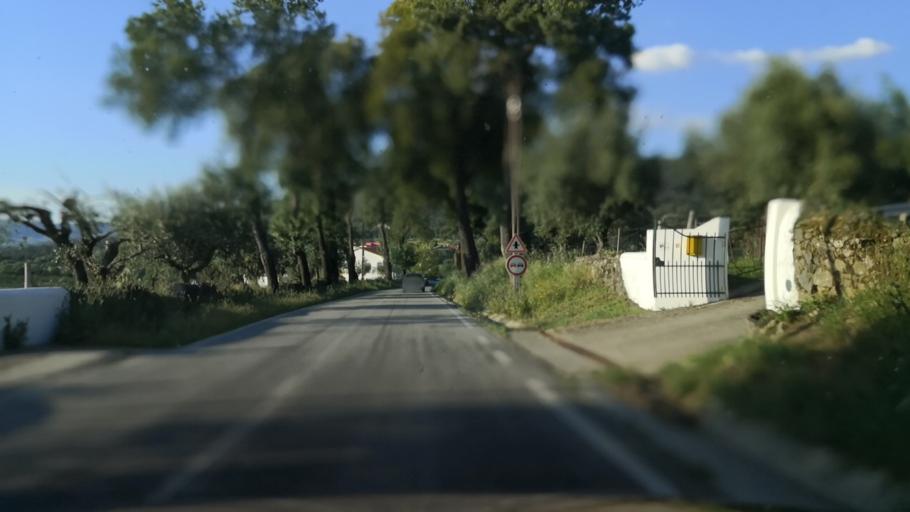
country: PT
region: Portalegre
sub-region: Portalegre
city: Portalegre
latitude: 39.3226
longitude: -7.4369
